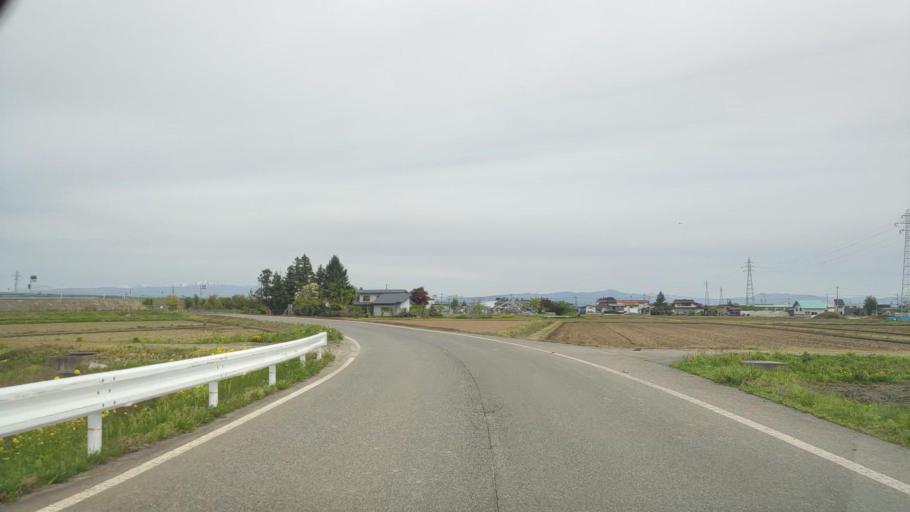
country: JP
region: Yamagata
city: Yonezawa
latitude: 37.9522
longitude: 140.1183
